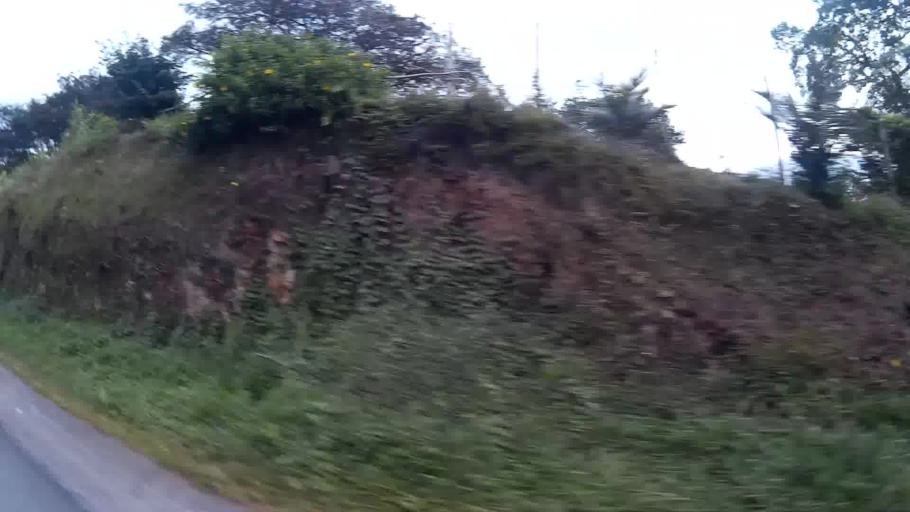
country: CO
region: Risaralda
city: Pereira
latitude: 4.7512
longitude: -75.6721
